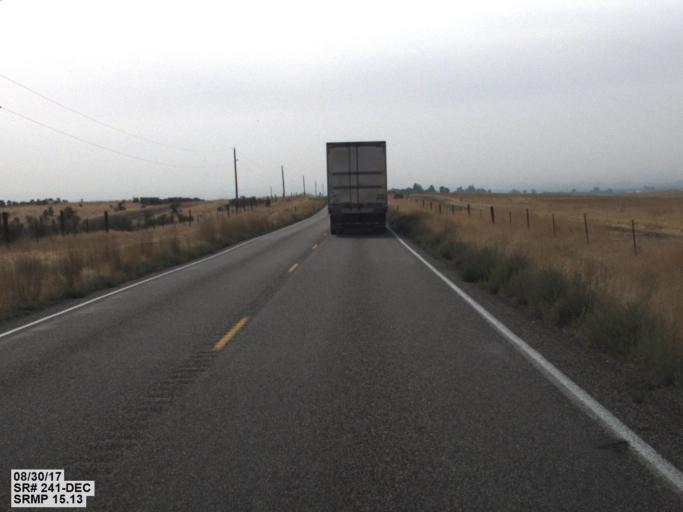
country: US
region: Washington
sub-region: Yakima County
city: Sunnyside
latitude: 46.4103
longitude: -119.9486
